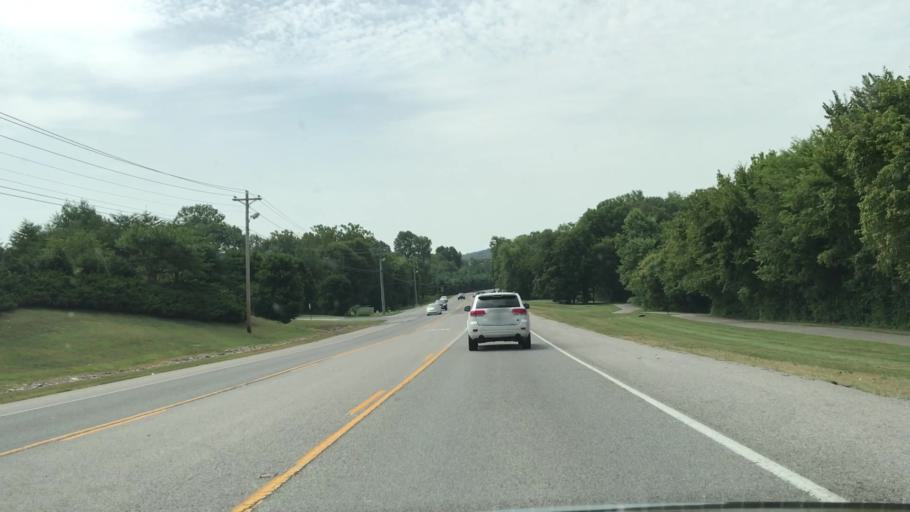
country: US
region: Tennessee
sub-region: Williamson County
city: Brentwood Estates
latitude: 35.9548
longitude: -86.7669
